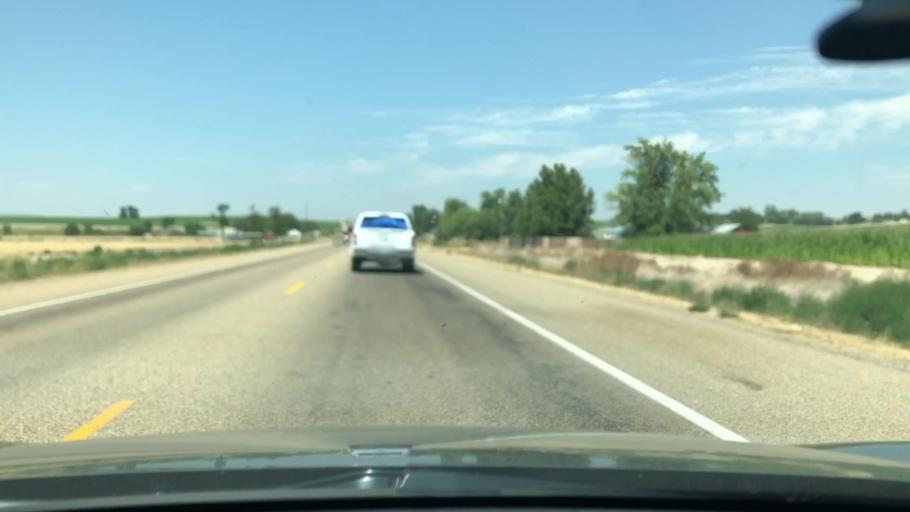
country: US
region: Idaho
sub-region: Canyon County
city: Parma
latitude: 43.8116
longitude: -116.9543
